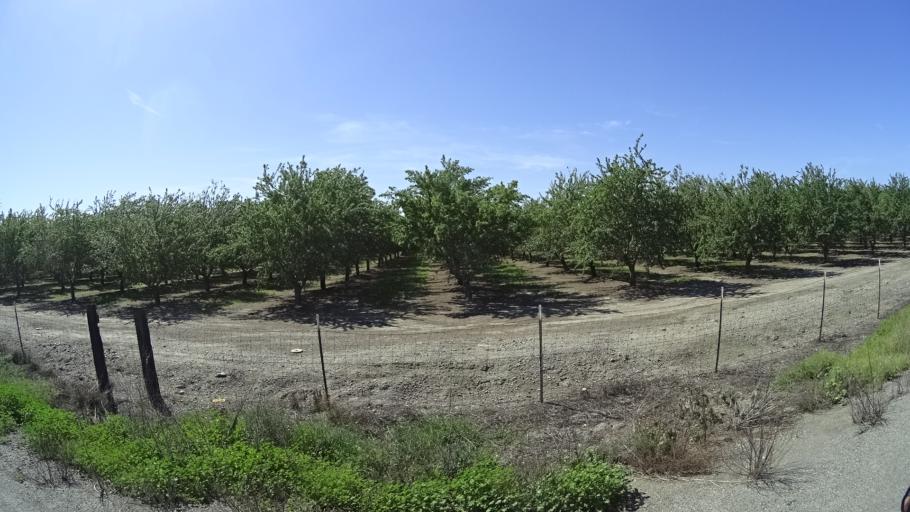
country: US
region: California
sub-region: Glenn County
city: Orland
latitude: 39.7394
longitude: -122.1101
